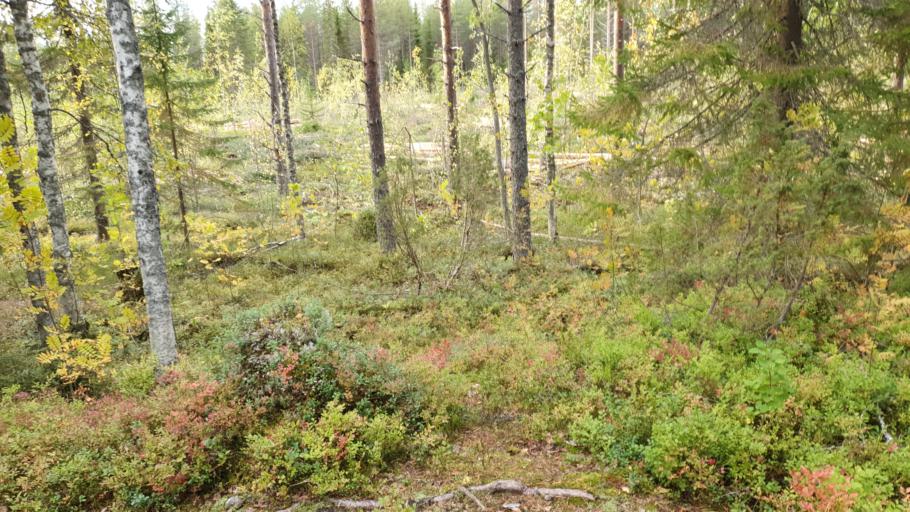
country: FI
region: North Karelia
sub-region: Pielisen Karjala
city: Lieksa
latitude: 63.9215
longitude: 30.1403
